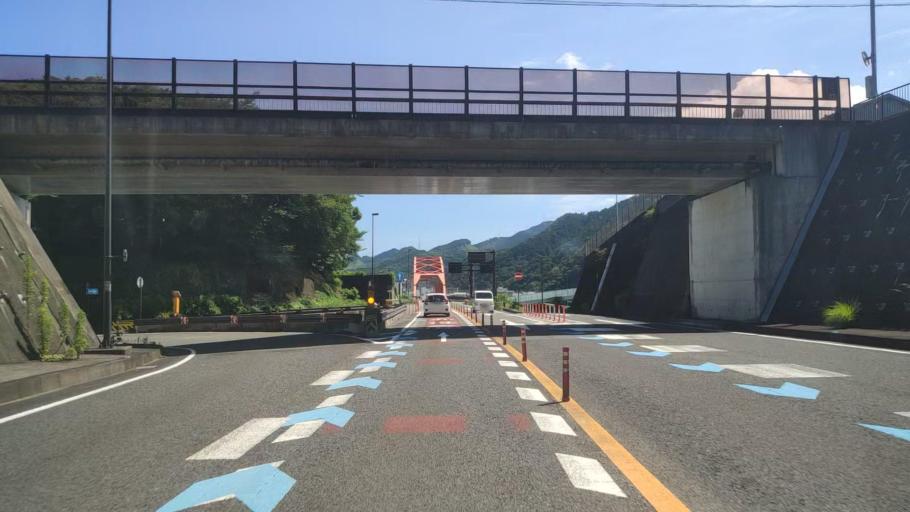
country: JP
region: Wakayama
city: Shingu
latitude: 33.7360
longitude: 135.9884
